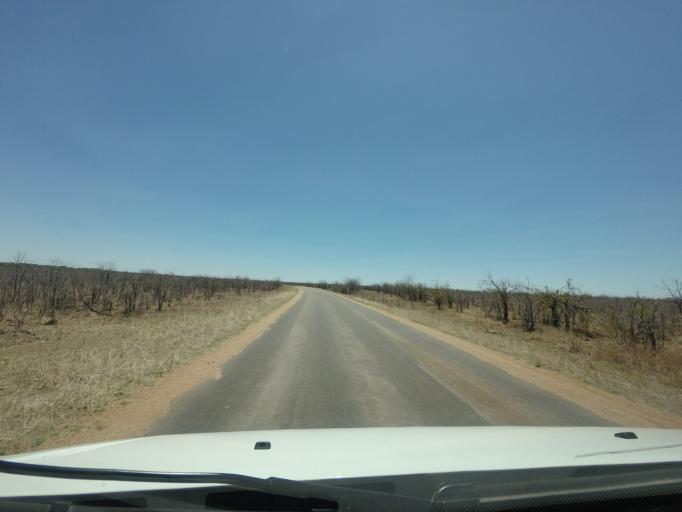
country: ZA
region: Limpopo
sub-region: Mopani District Municipality
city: Phalaborwa
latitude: -23.5655
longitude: 31.4524
